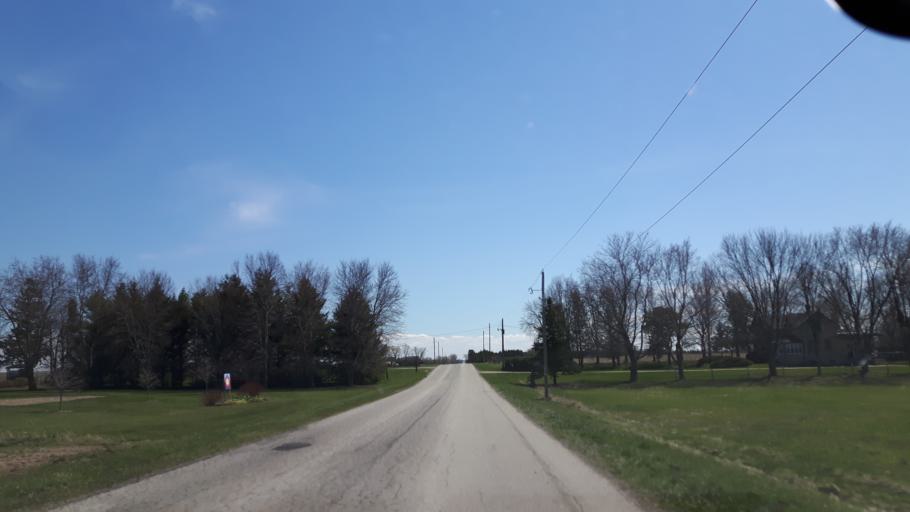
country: CA
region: Ontario
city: Goderich
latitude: 43.6269
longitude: -81.6440
